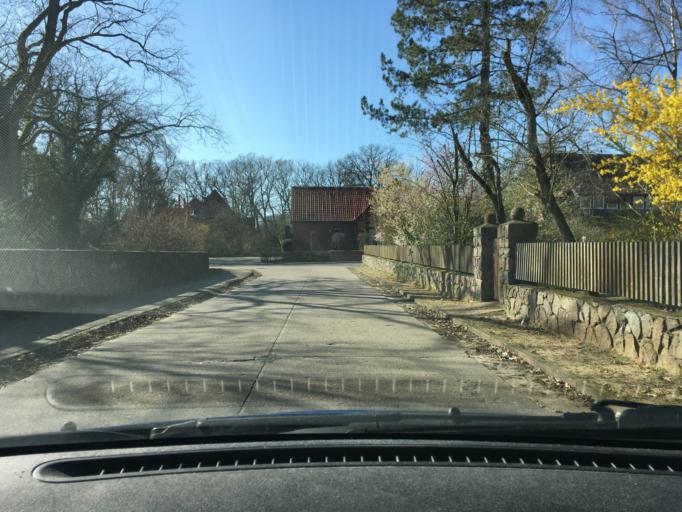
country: DE
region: Lower Saxony
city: Embsen
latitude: 53.1777
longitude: 10.3432
